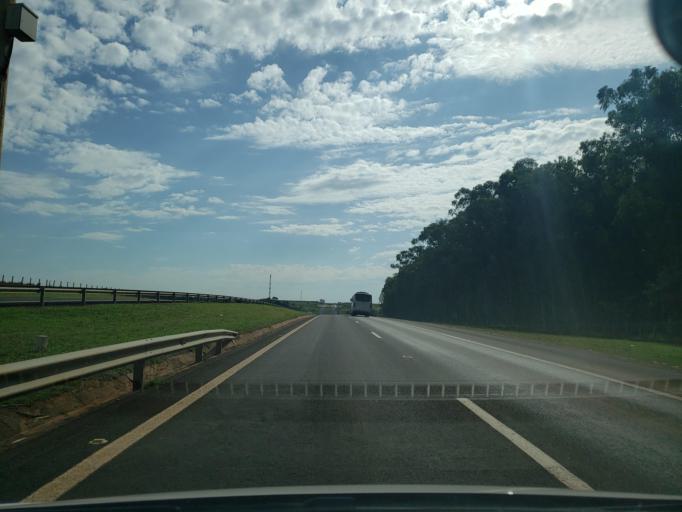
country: BR
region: Sao Paulo
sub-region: Promissao
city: Promissao
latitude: -21.6050
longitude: -49.8774
